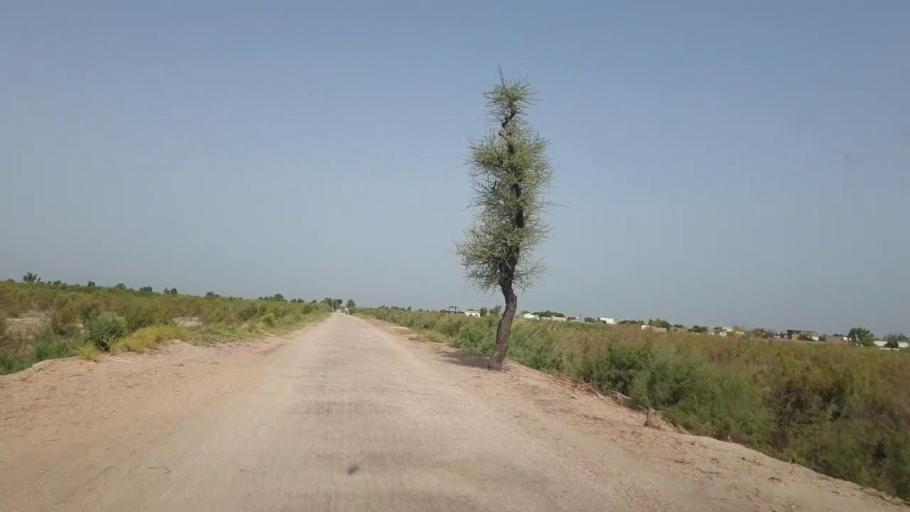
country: PK
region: Sindh
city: Sakrand
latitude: 26.3056
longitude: 68.2182
